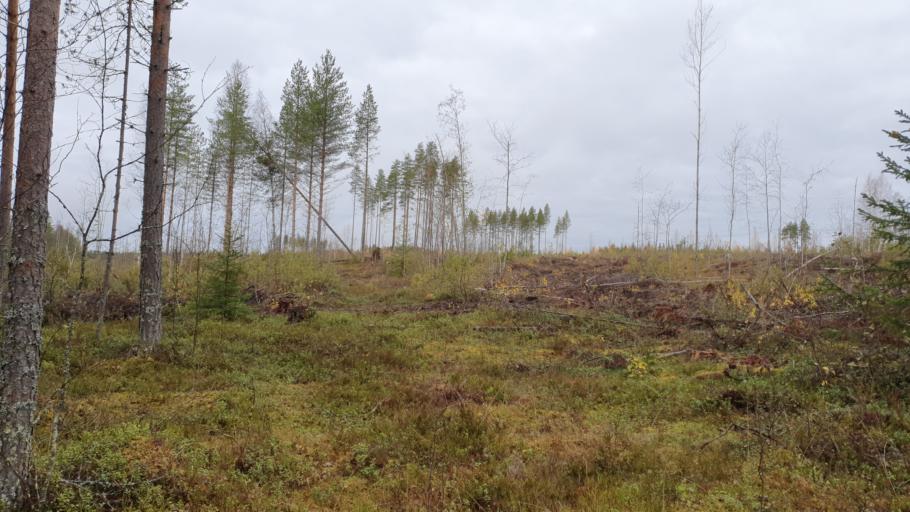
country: FI
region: Kainuu
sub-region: Kehys-Kainuu
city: Kuhmo
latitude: 64.1448
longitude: 29.4221
